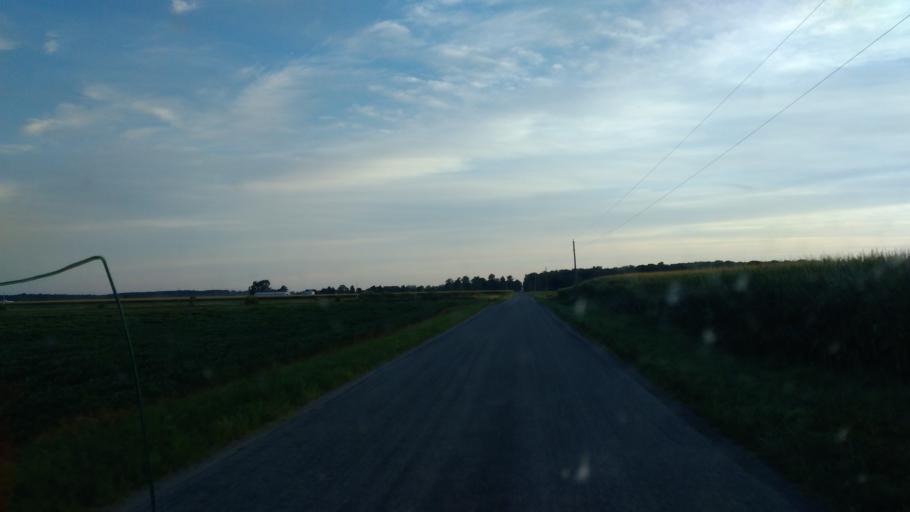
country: US
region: Indiana
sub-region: Adams County
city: Berne
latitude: 40.6670
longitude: -85.0324
